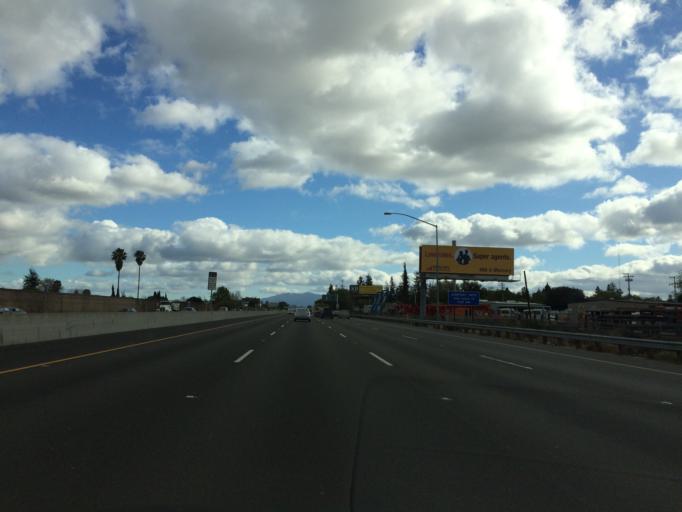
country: US
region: California
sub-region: Santa Clara County
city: Milpitas
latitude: 37.3957
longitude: -121.9077
